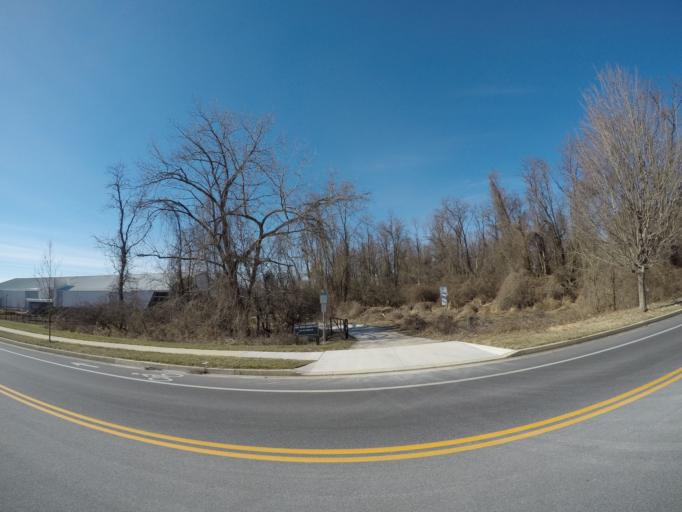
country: US
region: Maryland
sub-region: Howard County
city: Columbia
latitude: 39.2044
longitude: -76.8125
